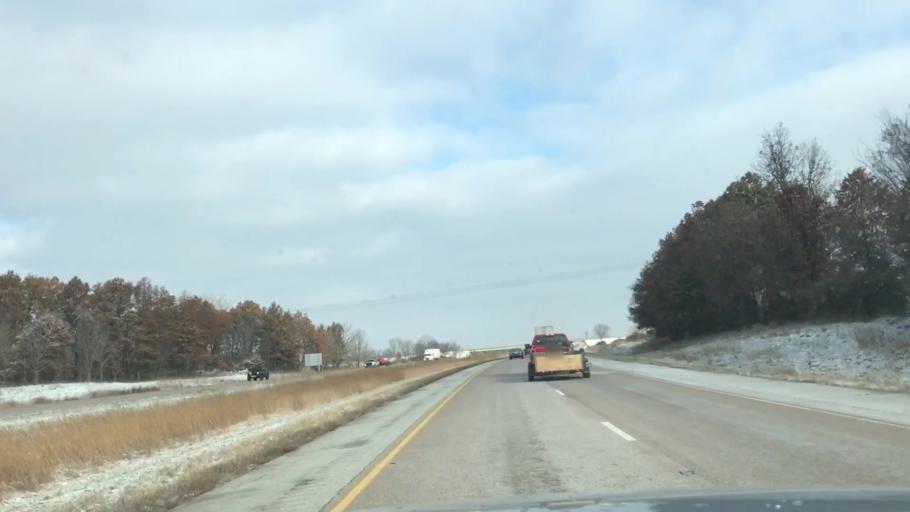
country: US
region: Illinois
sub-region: Macoupin County
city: Mount Olive
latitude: 39.0381
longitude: -89.7554
